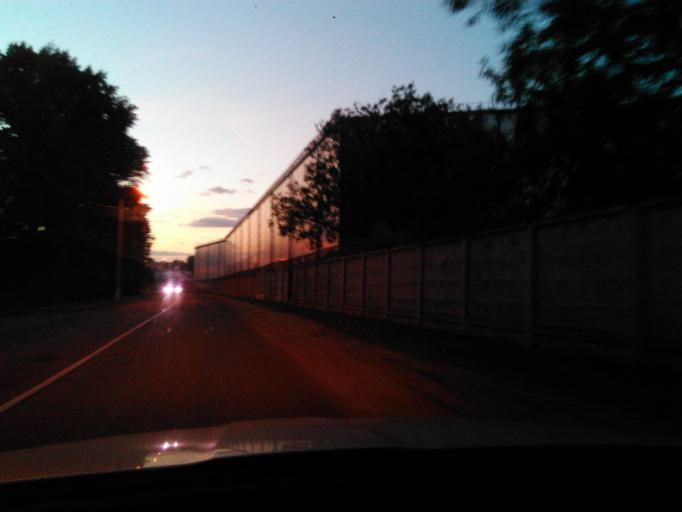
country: RU
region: Moskovskaya
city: Dolgoprudnyy
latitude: 55.9576
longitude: 37.5103
